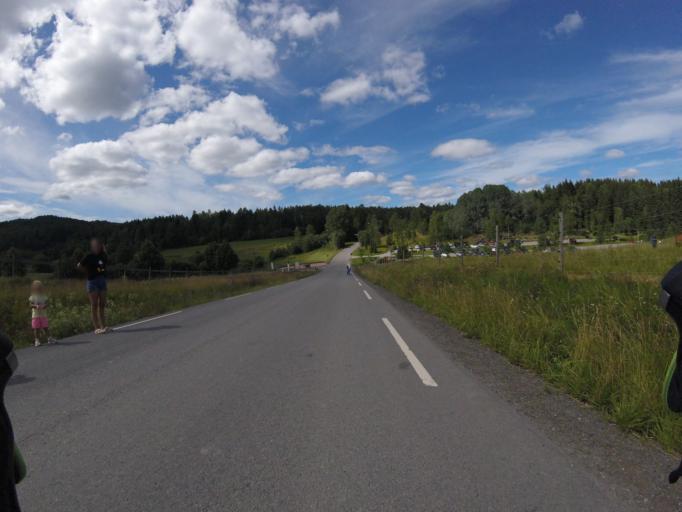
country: NO
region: Akershus
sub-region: Lorenskog
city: Kjenn
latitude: 59.8904
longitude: 10.9817
